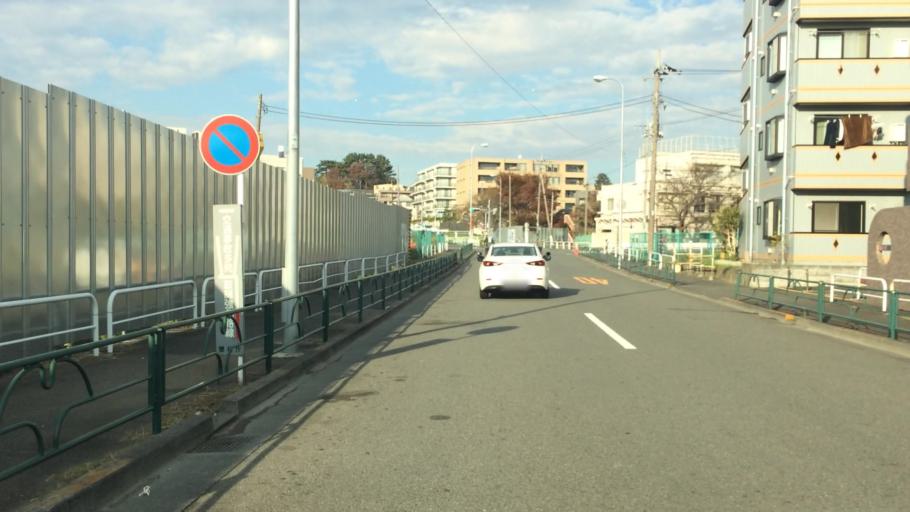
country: JP
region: Tokyo
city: Tokyo
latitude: 35.5992
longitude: 139.6463
